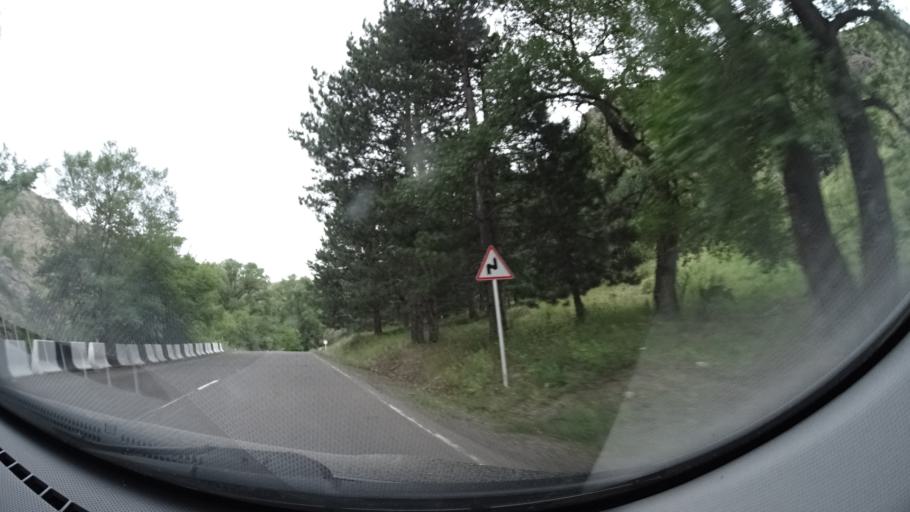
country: GE
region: Samtskhe-Javakheti
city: Akhaltsikhe
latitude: 41.6146
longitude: 43.0651
